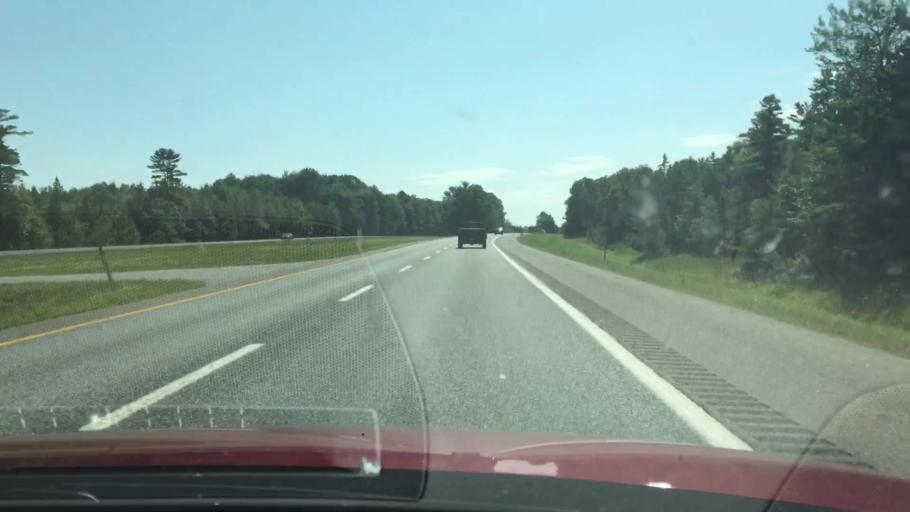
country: US
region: Maine
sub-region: Penobscot County
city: Orono
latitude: 44.8801
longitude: -68.6979
